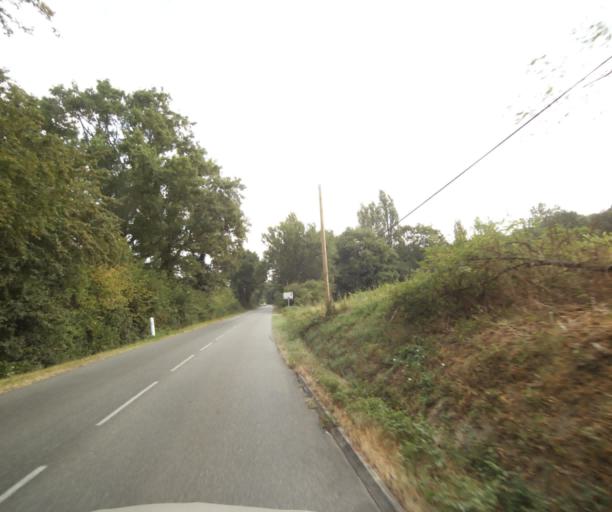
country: FR
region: Aquitaine
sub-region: Departement de la Gironde
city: Creon
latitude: 44.7633
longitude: -0.3621
